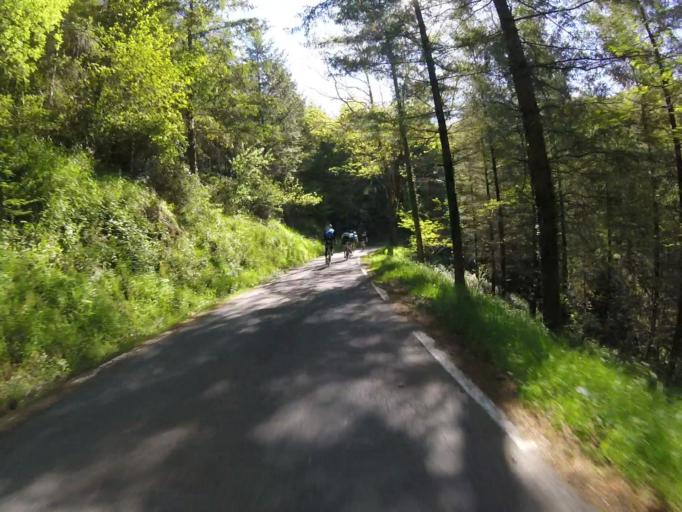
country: ES
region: Basque Country
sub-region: Provincia de Guipuzcoa
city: Errezil
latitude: 43.1908
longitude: -2.1946
